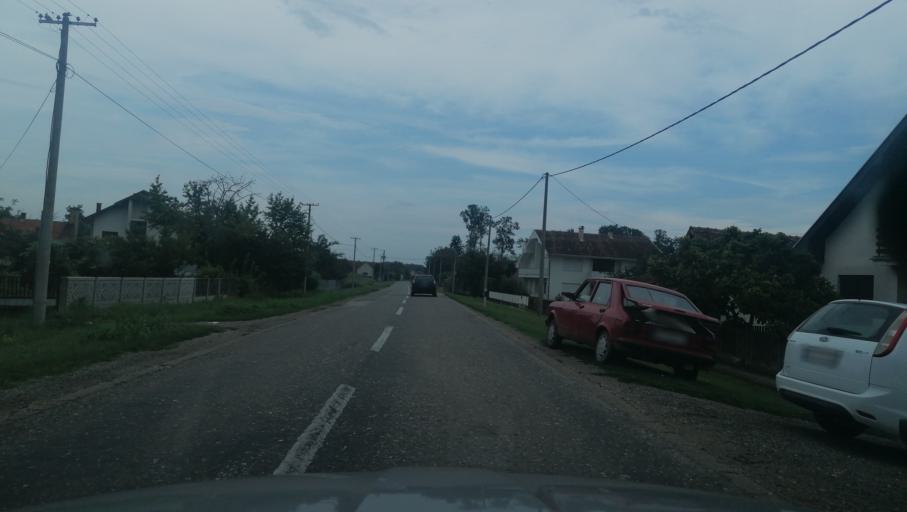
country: RS
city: Klenje
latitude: 44.8117
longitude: 19.4412
